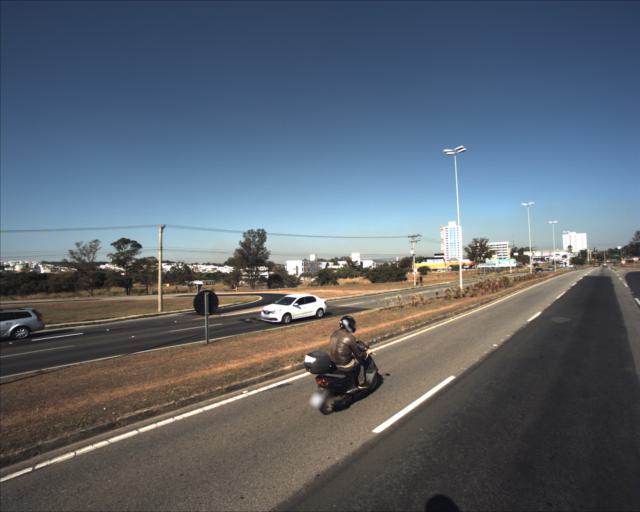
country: BR
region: Sao Paulo
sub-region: Sorocaba
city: Sorocaba
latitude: -23.4701
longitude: -47.4238
